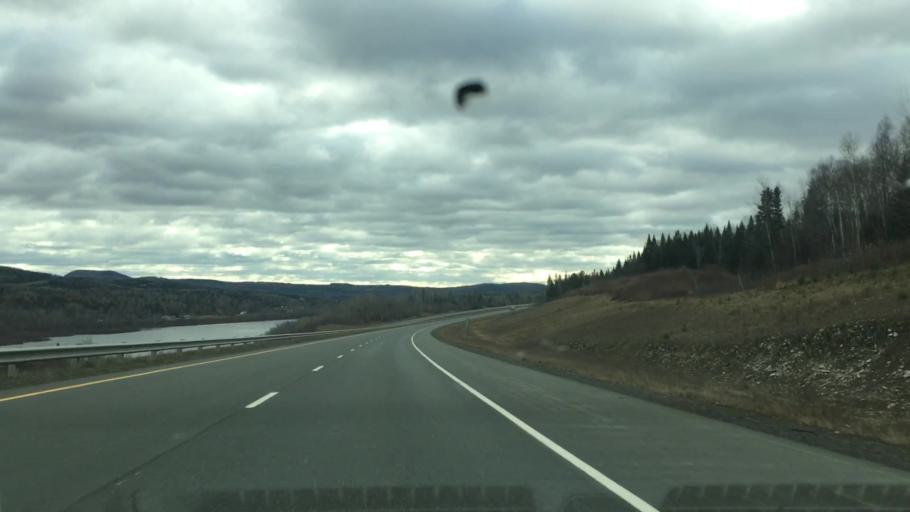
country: US
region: Maine
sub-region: Aroostook County
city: Fort Fairfield
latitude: 46.6814
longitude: -67.7323
